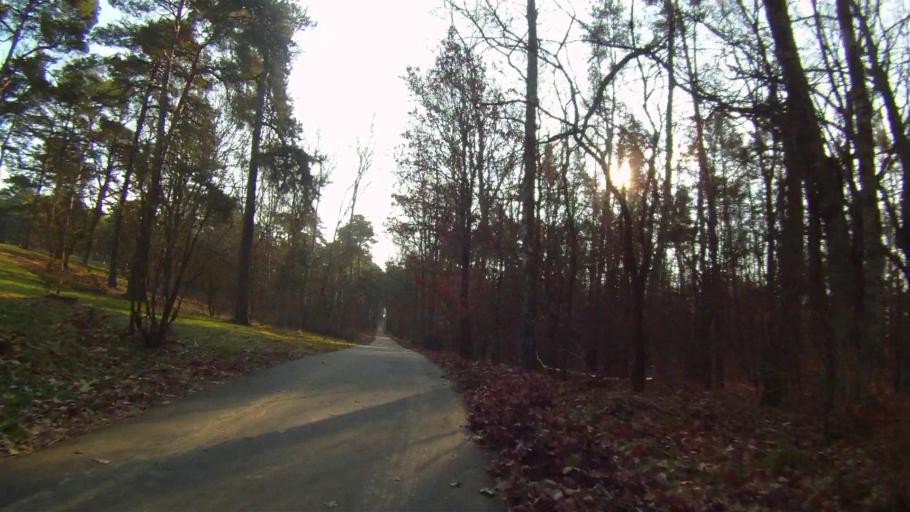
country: DE
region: Berlin
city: Rahnsdorf
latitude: 52.4278
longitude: 13.6762
